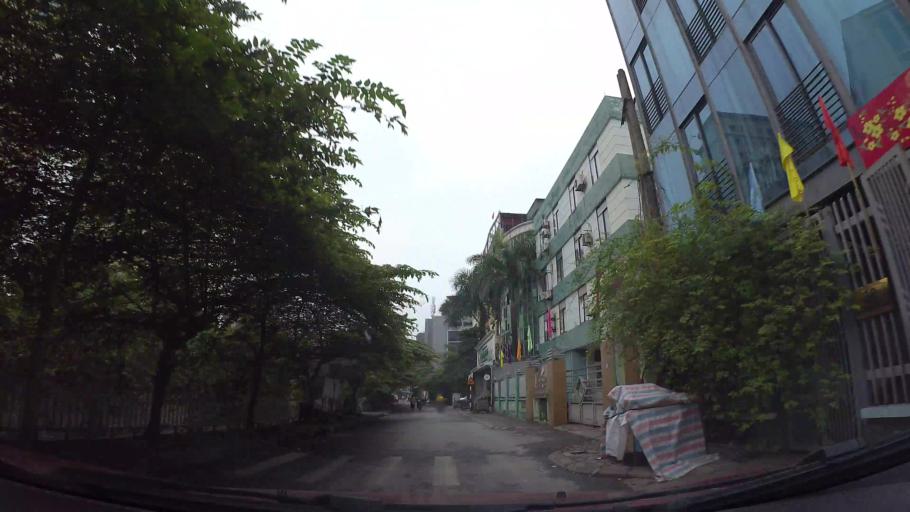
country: VN
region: Ha Noi
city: Hai BaTrung
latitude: 21.0003
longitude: 105.8354
